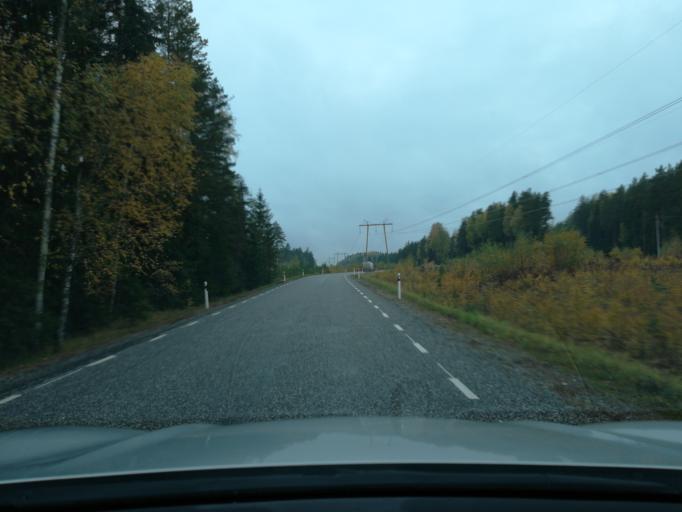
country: EE
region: Ida-Virumaa
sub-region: Johvi vald
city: Johvi
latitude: 59.1600
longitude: 27.4167
